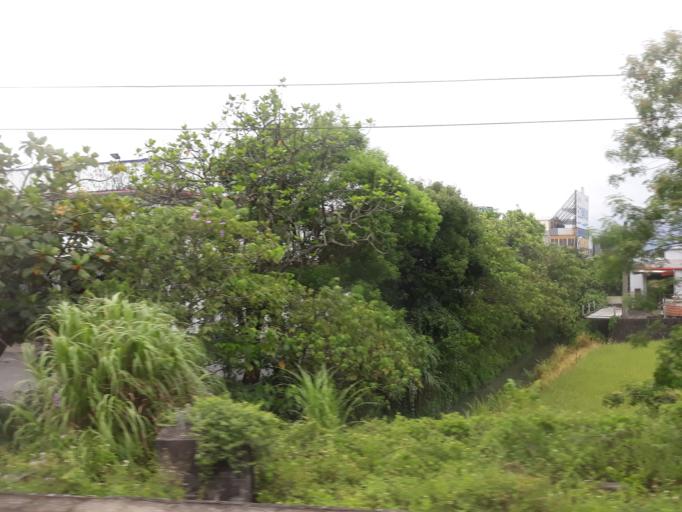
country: TW
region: Taiwan
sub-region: Yilan
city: Yilan
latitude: 24.7092
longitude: 121.7736
